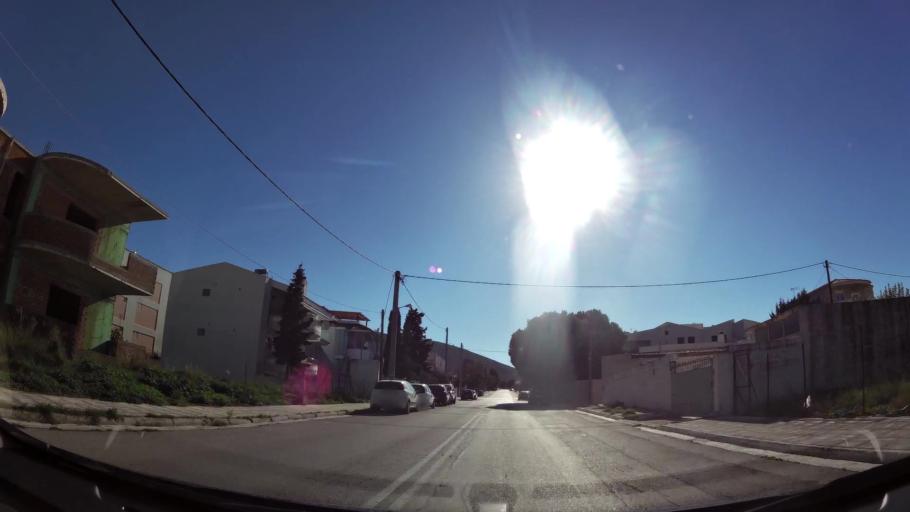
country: GR
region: Attica
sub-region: Nomarchia Anatolikis Attikis
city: Kalyvia Thorikou
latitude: 37.8375
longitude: 23.9328
